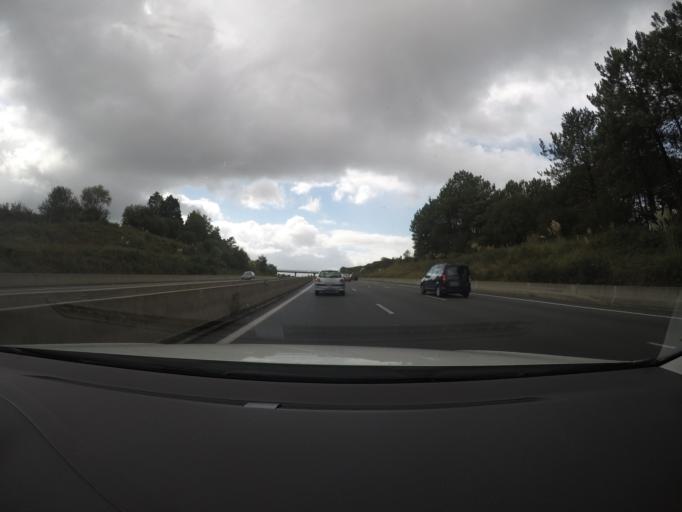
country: FR
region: Aquitaine
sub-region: Departement des Pyrenees-Atlantiques
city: Boucau
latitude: 43.5271
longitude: -1.4378
